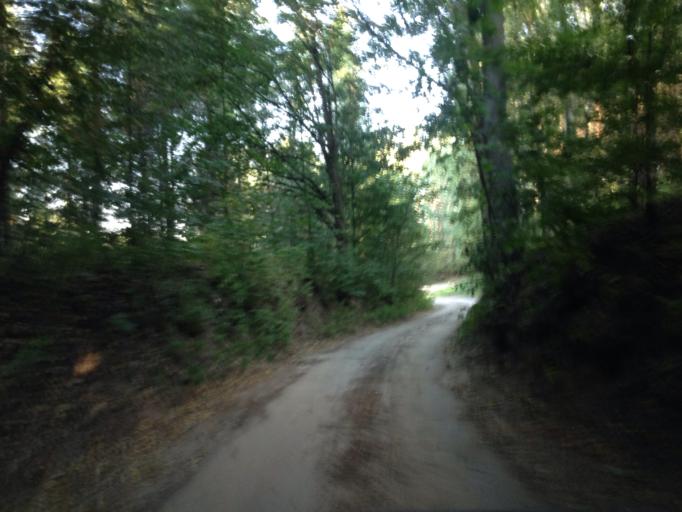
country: PL
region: Kujawsko-Pomorskie
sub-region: Powiat brodnicki
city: Gorzno
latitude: 53.2249
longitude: 19.7351
